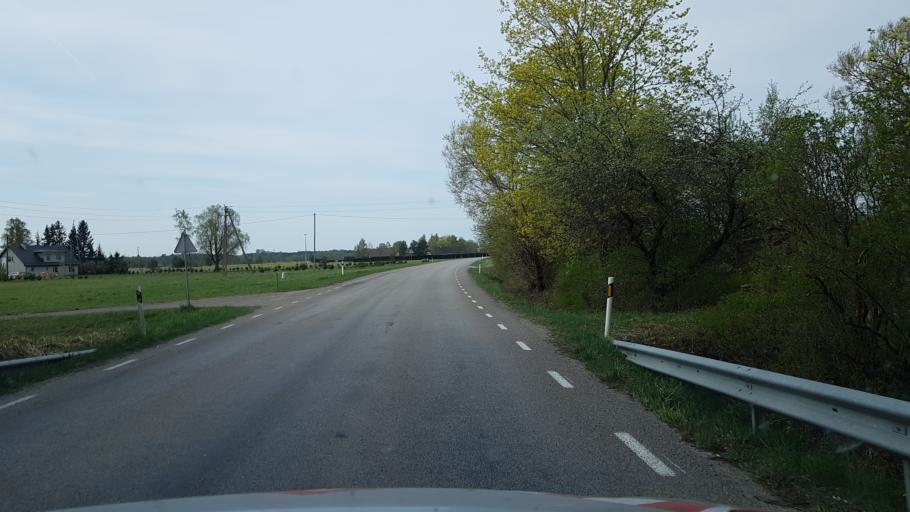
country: EE
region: Paernumaa
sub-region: Audru vald
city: Audru
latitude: 58.3697
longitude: 24.2682
